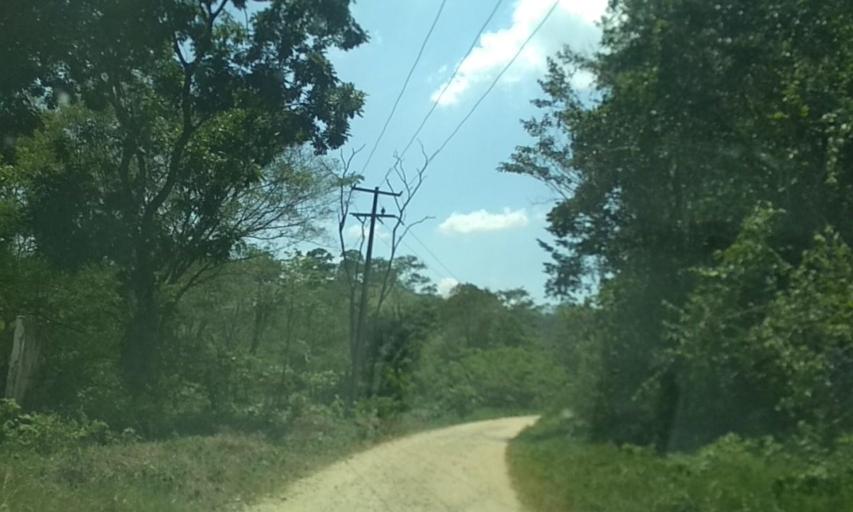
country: MX
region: Chiapas
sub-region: Tecpatan
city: Raudales Malpaso
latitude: 17.2808
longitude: -93.8292
